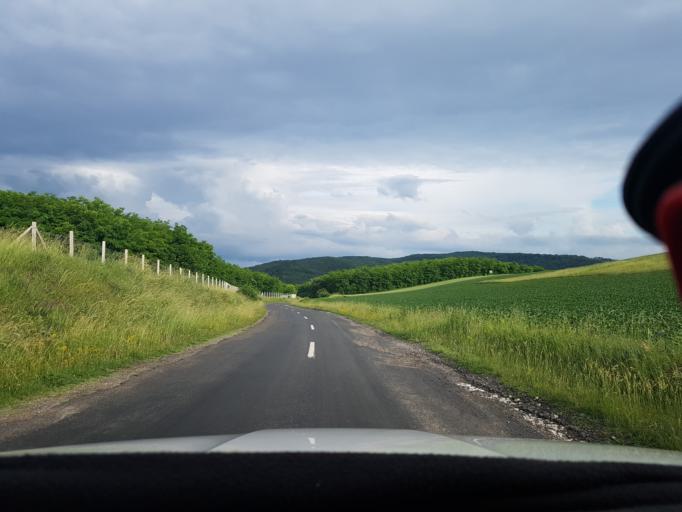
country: HU
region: Komarom-Esztergom
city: Nyergesujfalu
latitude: 47.7202
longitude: 18.5520
